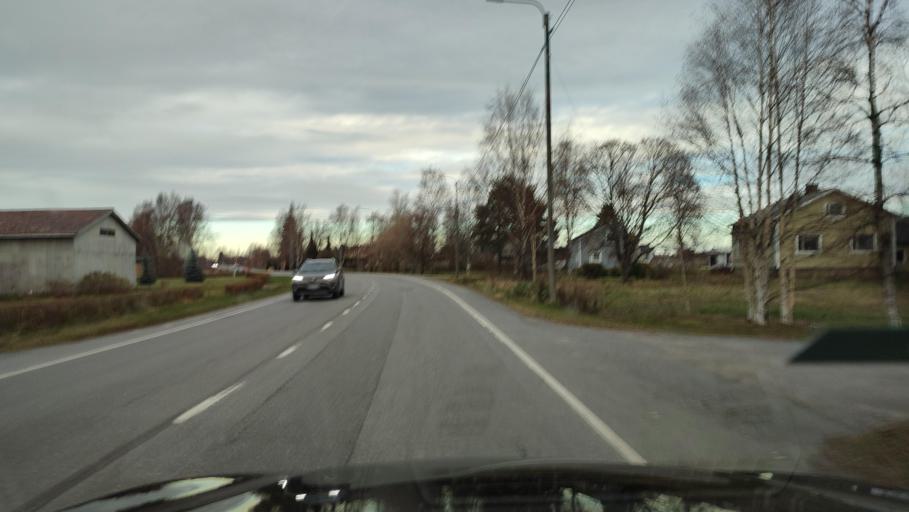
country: FI
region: Ostrobothnia
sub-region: Sydosterbotten
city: Naerpes
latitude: 62.4612
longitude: 21.3563
